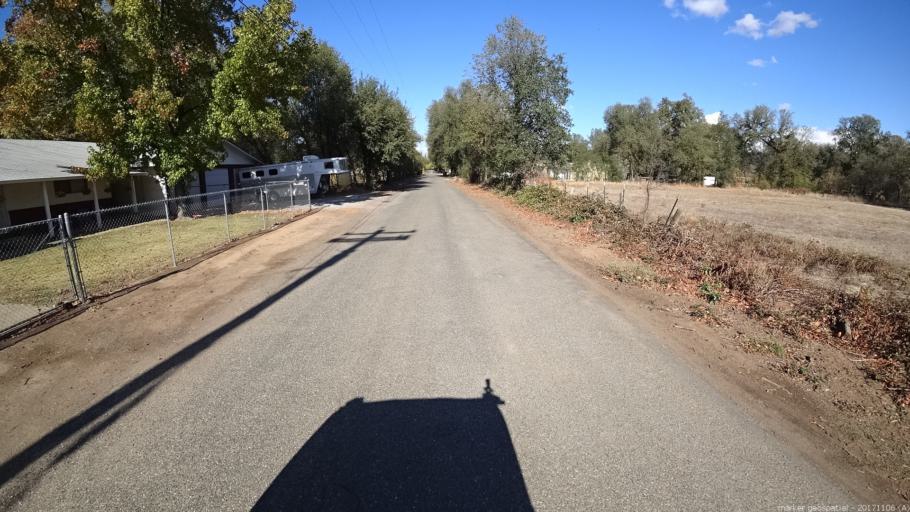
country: US
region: California
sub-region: Shasta County
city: Palo Cedro
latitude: 40.5788
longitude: -122.2958
